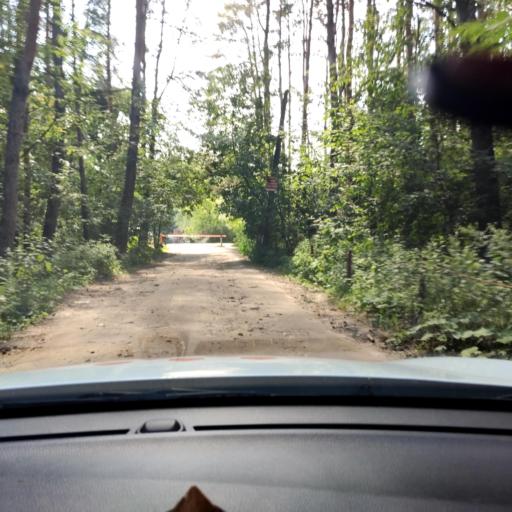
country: RU
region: Tatarstan
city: Osinovo
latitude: 55.8281
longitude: 48.7818
